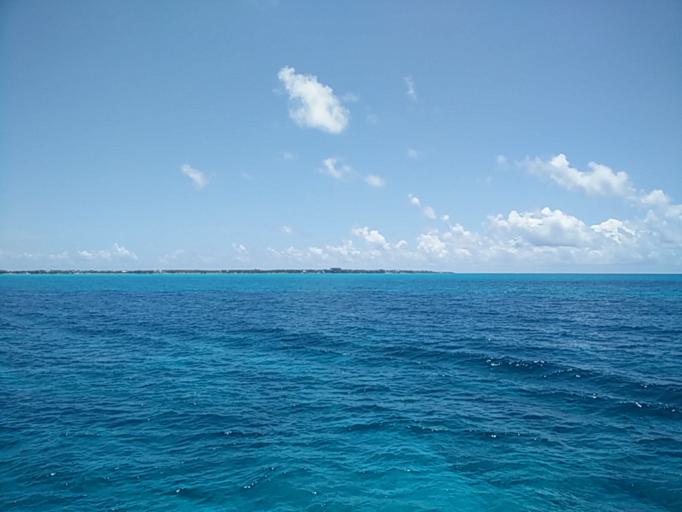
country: MX
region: Quintana Roo
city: Isla Mujeres
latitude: 21.2045
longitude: -86.7595
